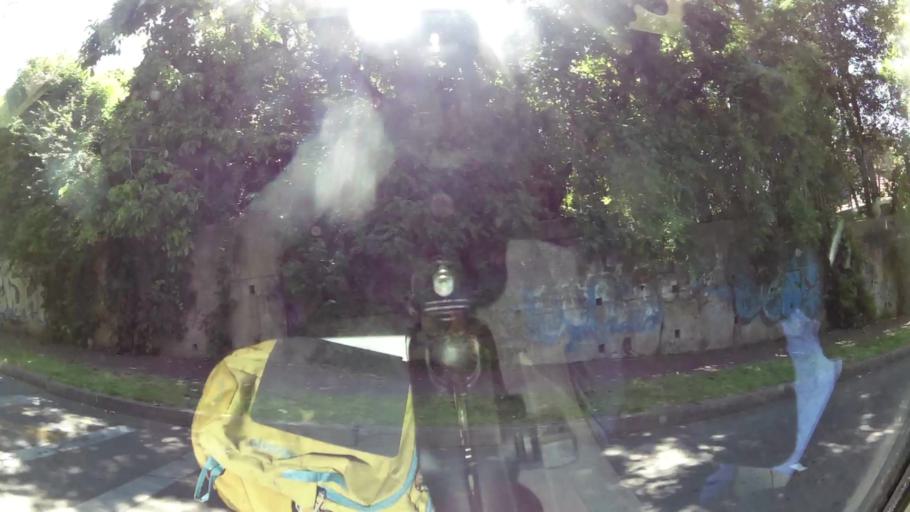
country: AR
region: Buenos Aires
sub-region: Partido de San Isidro
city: San Isidro
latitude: -34.4713
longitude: -58.4992
